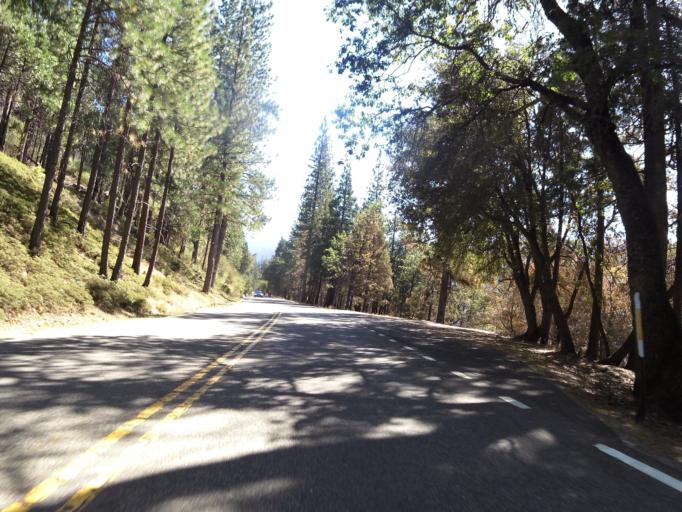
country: US
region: California
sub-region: Mariposa County
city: Yosemite Valley
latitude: 37.5705
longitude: -119.6913
